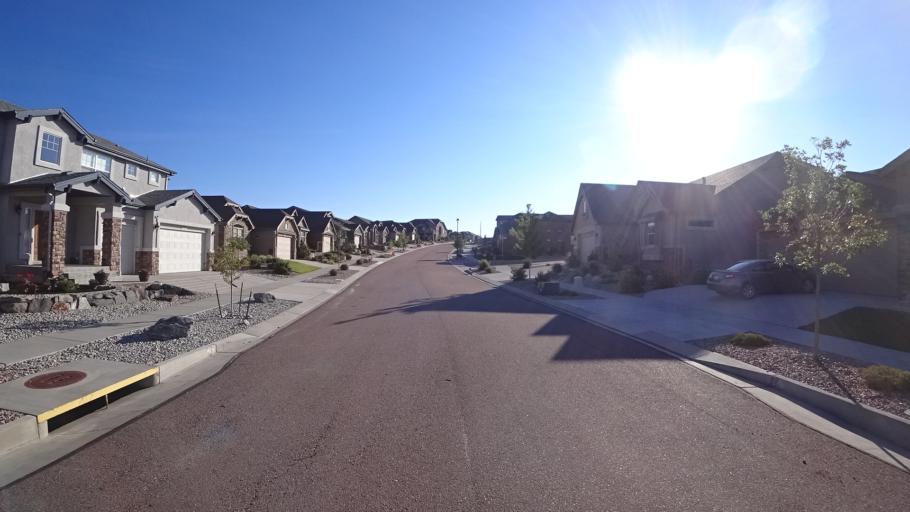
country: US
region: Colorado
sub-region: El Paso County
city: Black Forest
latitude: 38.9832
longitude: -104.7711
